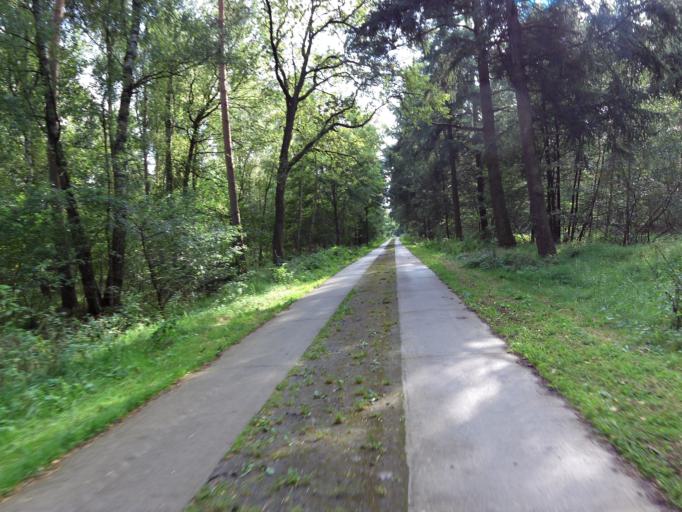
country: DE
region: Saxony-Anhalt
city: Sandau
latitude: 52.8064
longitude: 12.0551
